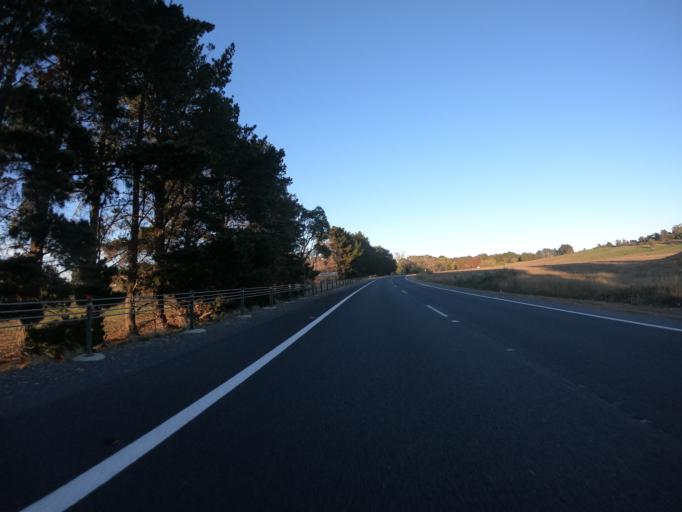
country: AU
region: New South Wales
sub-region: Goulburn Mulwaree
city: Goulburn
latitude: -34.8911
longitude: 149.5271
